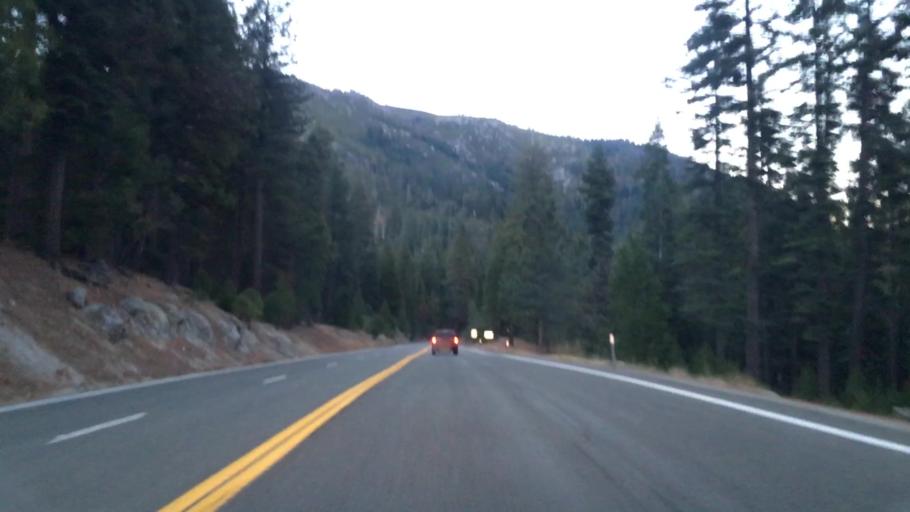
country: US
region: California
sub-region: El Dorado County
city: South Lake Tahoe
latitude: 38.7892
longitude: -120.1981
